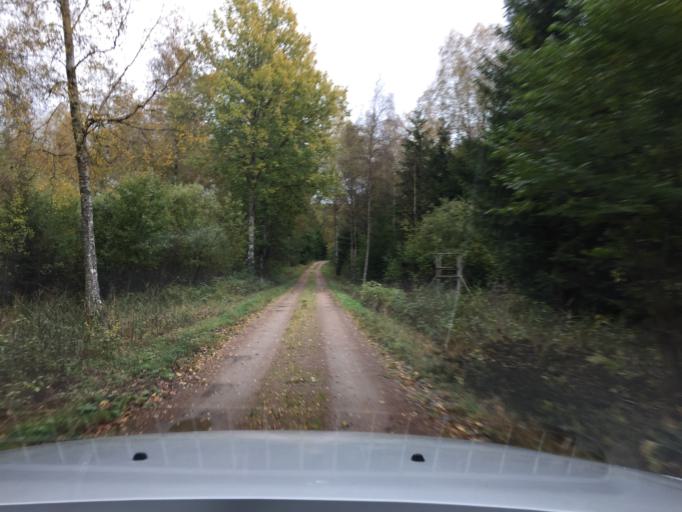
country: SE
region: Skane
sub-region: Hassleholms Kommun
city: Tormestorp
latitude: 56.0539
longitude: 13.7466
